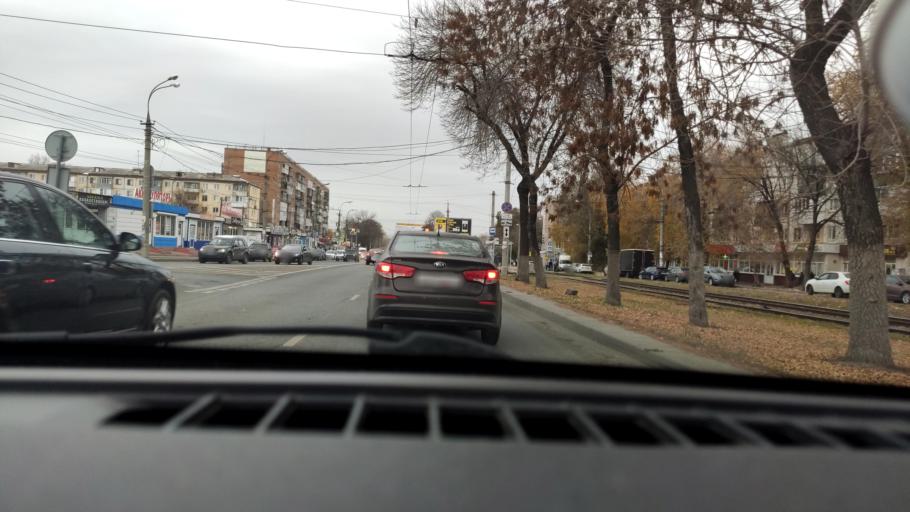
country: RU
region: Samara
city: Samara
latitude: 53.2120
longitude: 50.1960
